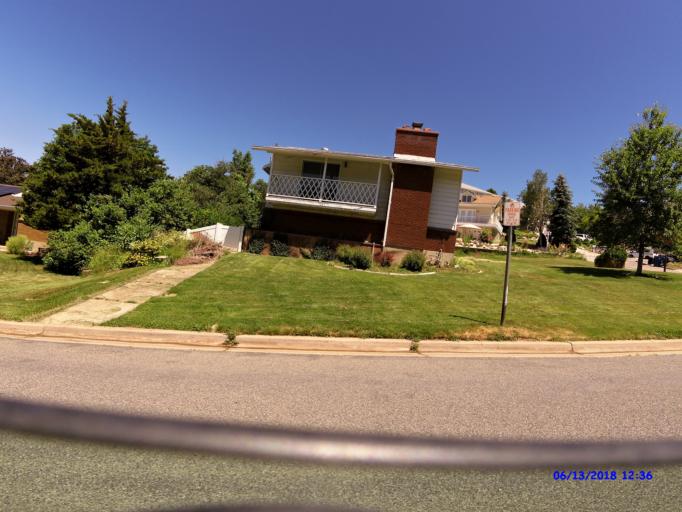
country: US
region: Utah
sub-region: Weber County
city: South Ogden
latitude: 41.1990
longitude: -111.9404
